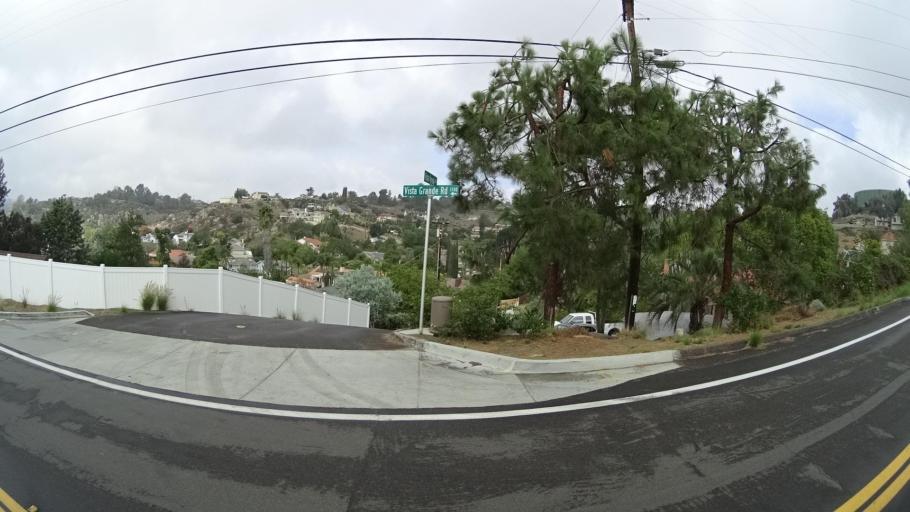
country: US
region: California
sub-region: San Diego County
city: Rancho San Diego
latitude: 32.7675
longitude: -116.9128
